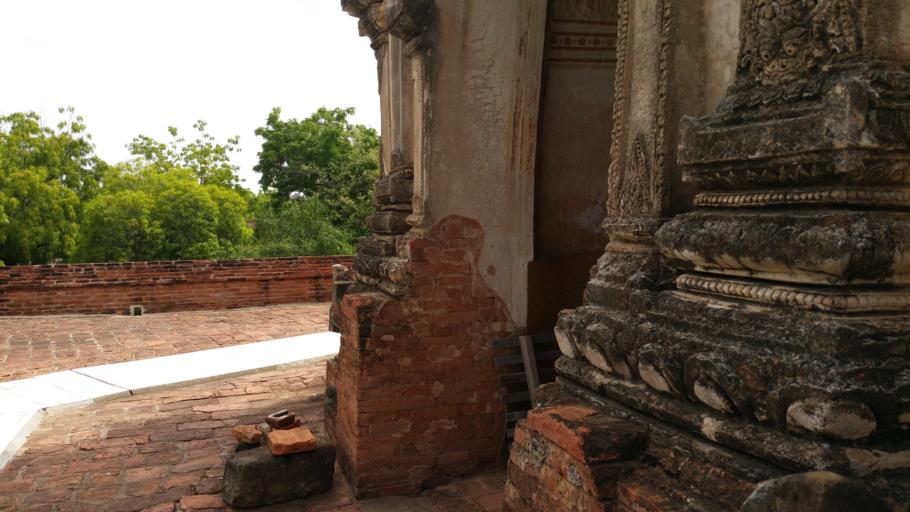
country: MM
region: Magway
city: Chauk
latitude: 21.1452
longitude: 94.8830
